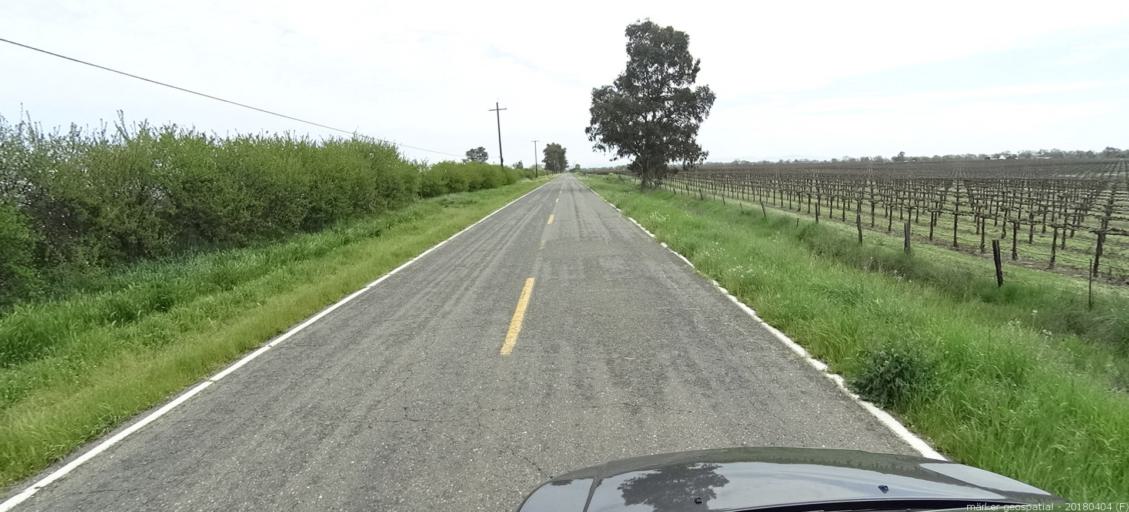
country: US
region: California
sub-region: Sacramento County
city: Herald
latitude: 38.2634
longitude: -121.1874
